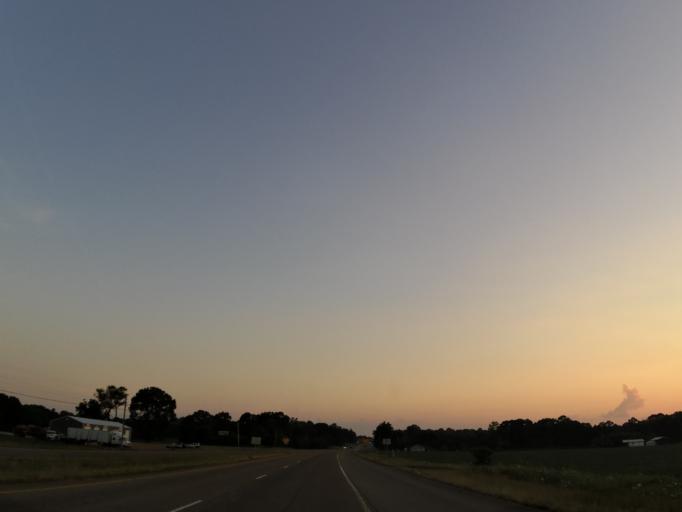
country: US
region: Tennessee
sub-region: Carroll County
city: McKenzie
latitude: 36.1480
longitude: -88.4764
